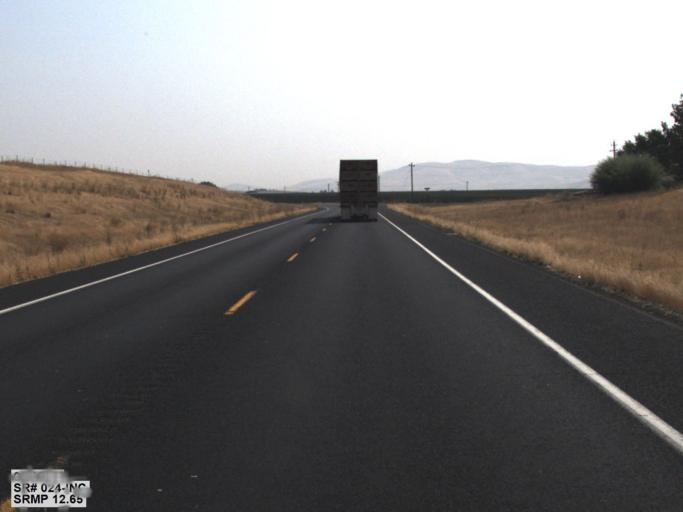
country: US
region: Washington
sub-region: Yakima County
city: Zillah
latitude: 46.5214
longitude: -120.2356
